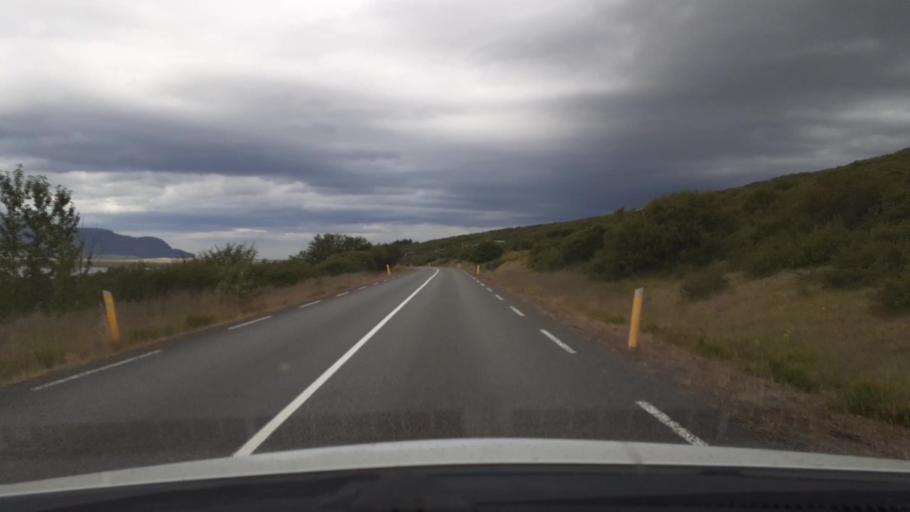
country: IS
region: West
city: Borgarnes
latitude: 64.5427
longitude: -21.5589
